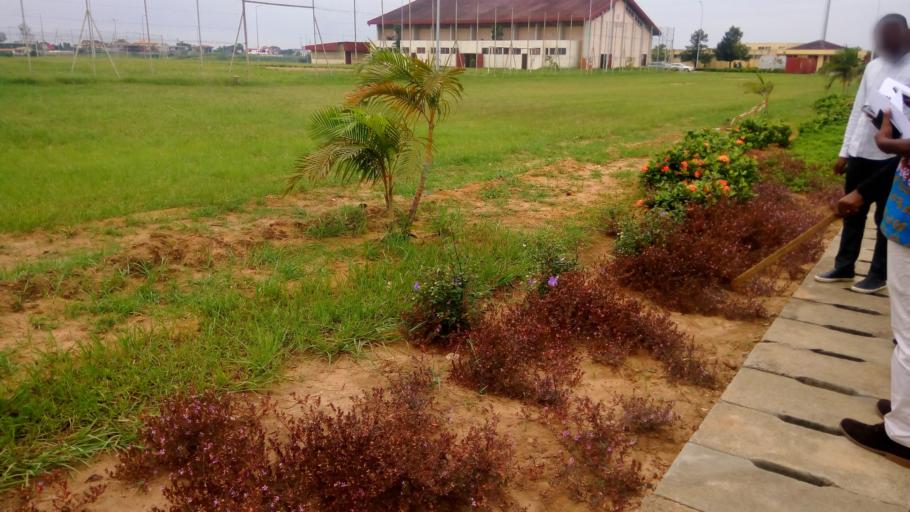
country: CI
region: Lagunes
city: Abidjan
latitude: 5.3400
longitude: -3.9880
